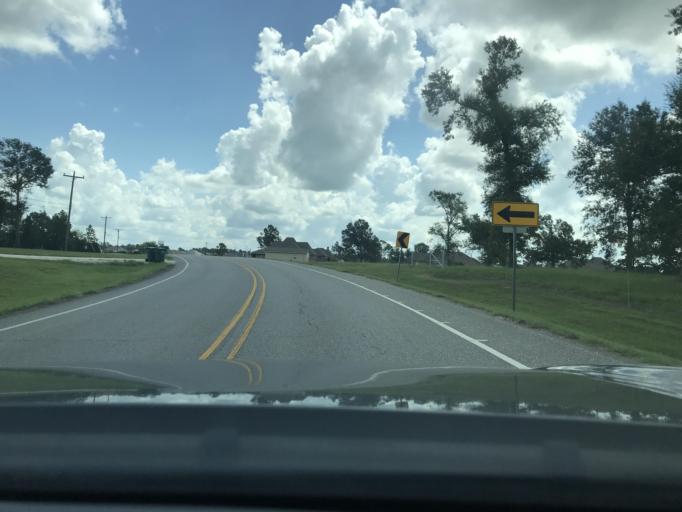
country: US
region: Louisiana
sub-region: Calcasieu Parish
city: Moss Bluff
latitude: 30.3398
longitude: -93.2457
